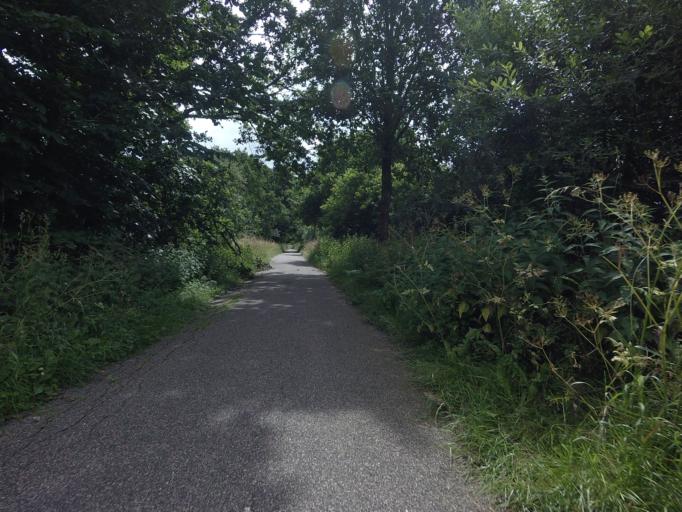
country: DK
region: Central Jutland
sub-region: Randers Kommune
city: Langa
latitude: 56.3700
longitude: 9.8998
